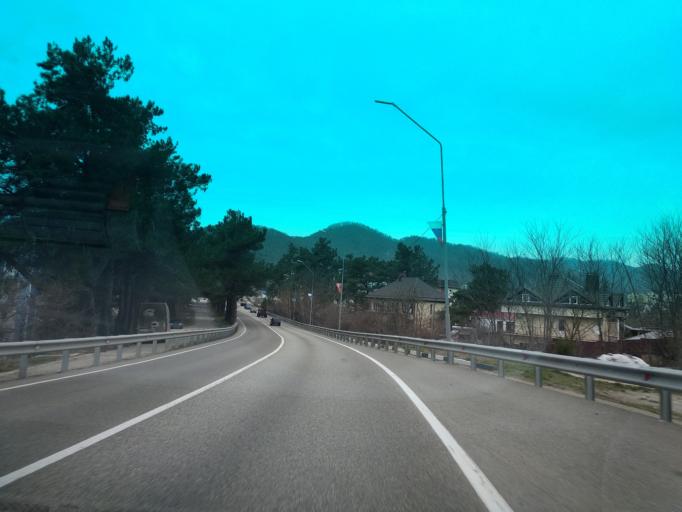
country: RU
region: Krasnodarskiy
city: Ol'ginka
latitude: 44.1970
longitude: 38.8914
